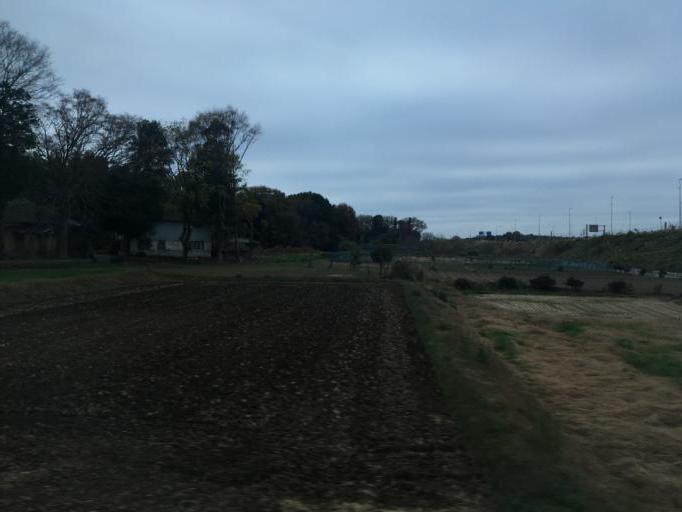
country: JP
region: Ibaraki
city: Yuki
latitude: 36.3021
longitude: 139.8440
